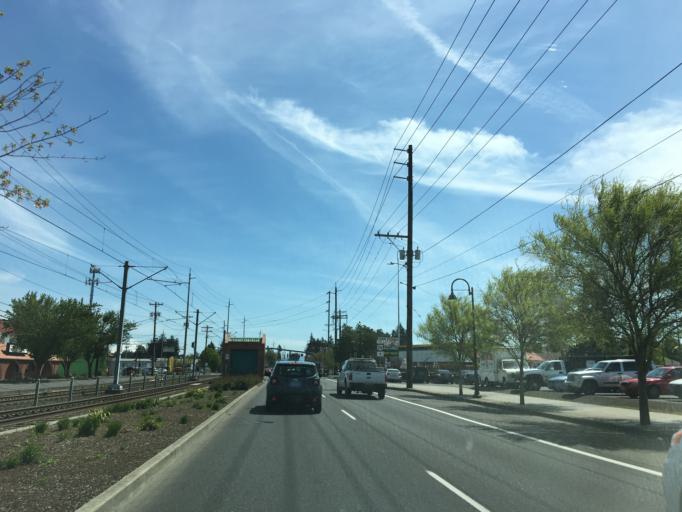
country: US
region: Oregon
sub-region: Multnomah County
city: Fairview
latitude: 45.5201
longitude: -122.4700
